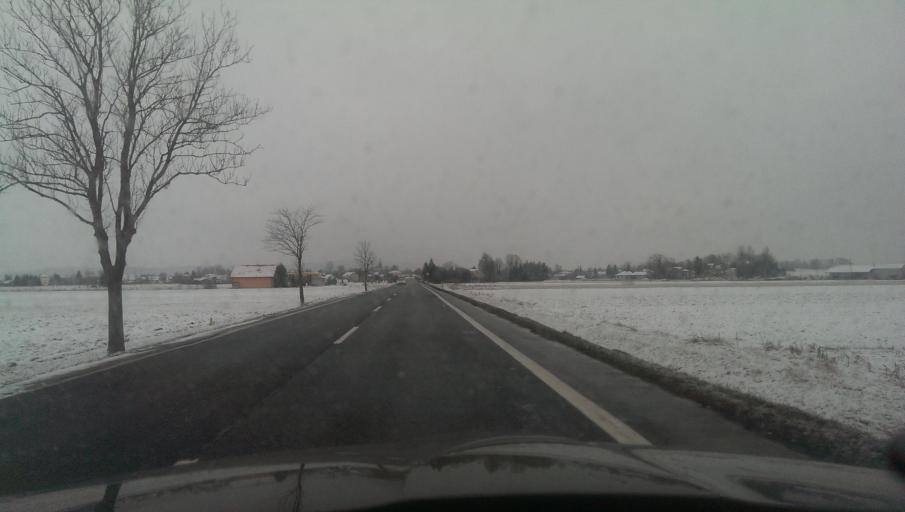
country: PL
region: Subcarpathian Voivodeship
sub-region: Powiat sanocki
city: Zarszyn
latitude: 49.5824
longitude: 21.9964
